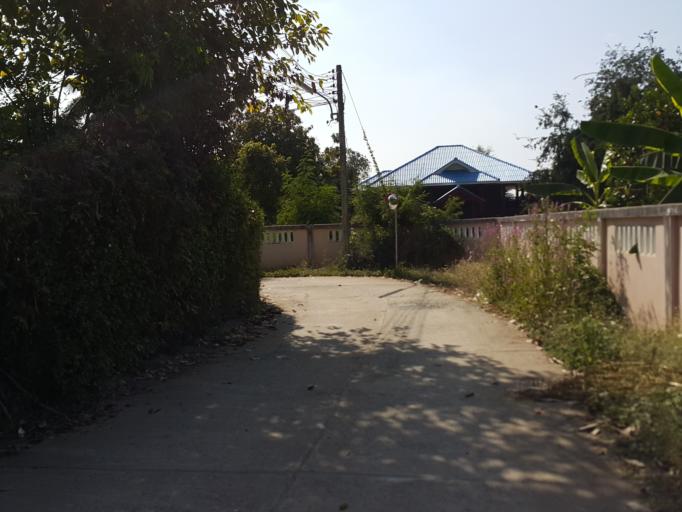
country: TH
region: Chiang Mai
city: San Kamphaeng
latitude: 18.8141
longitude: 99.1599
